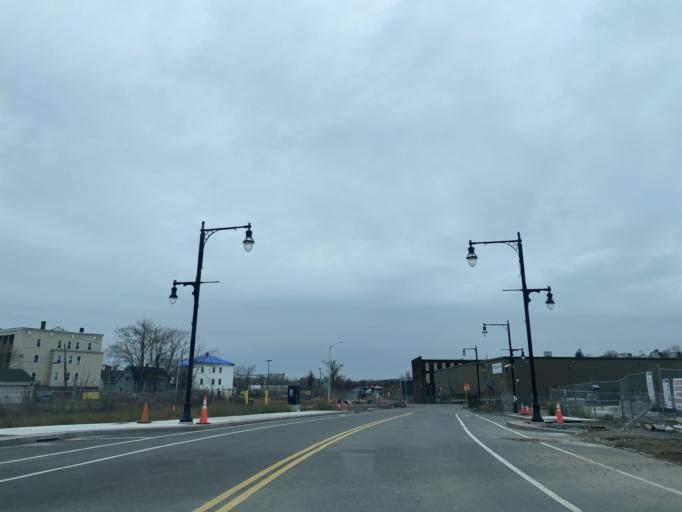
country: US
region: Massachusetts
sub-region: Worcester County
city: Worcester
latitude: 42.2549
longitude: -71.8023
